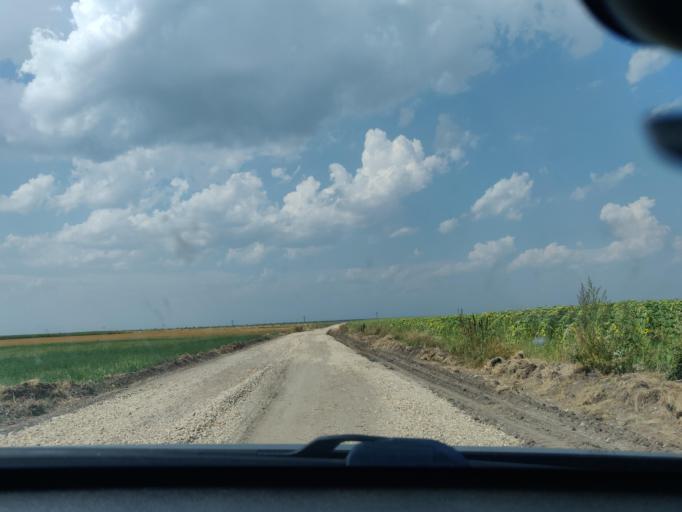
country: RO
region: Teleorman
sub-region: Comuna Sarbeni
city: Sarbeni
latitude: 44.5041
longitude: 25.3973
